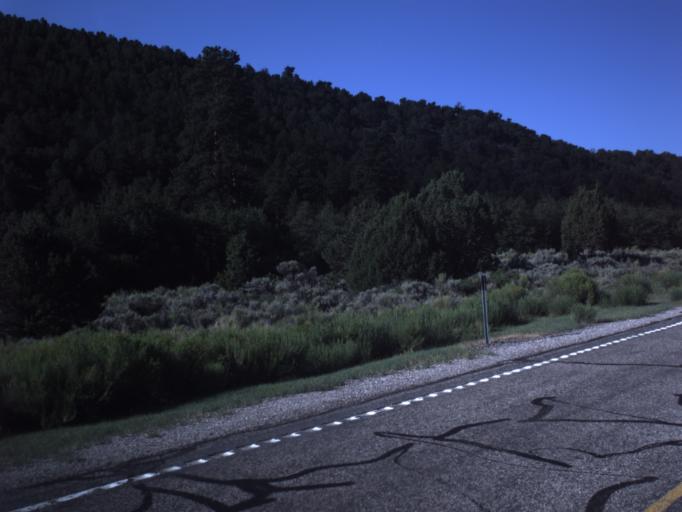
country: US
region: Utah
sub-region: Wayne County
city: Loa
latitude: 38.6517
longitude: -111.4359
